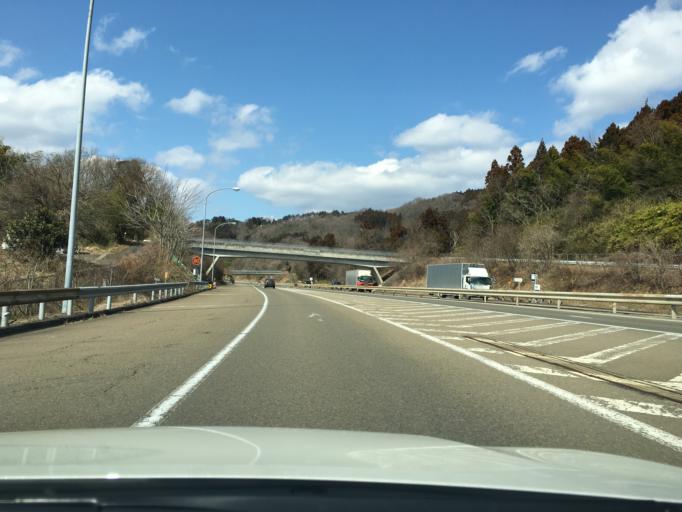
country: JP
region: Miyagi
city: Okawara
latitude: 38.1414
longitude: 140.7216
